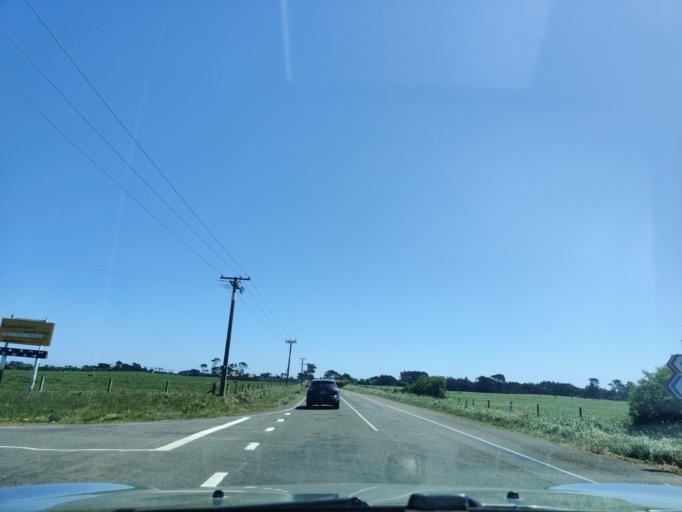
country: NZ
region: Taranaki
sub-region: South Taranaki District
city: Hawera
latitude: -39.5460
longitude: 174.0787
